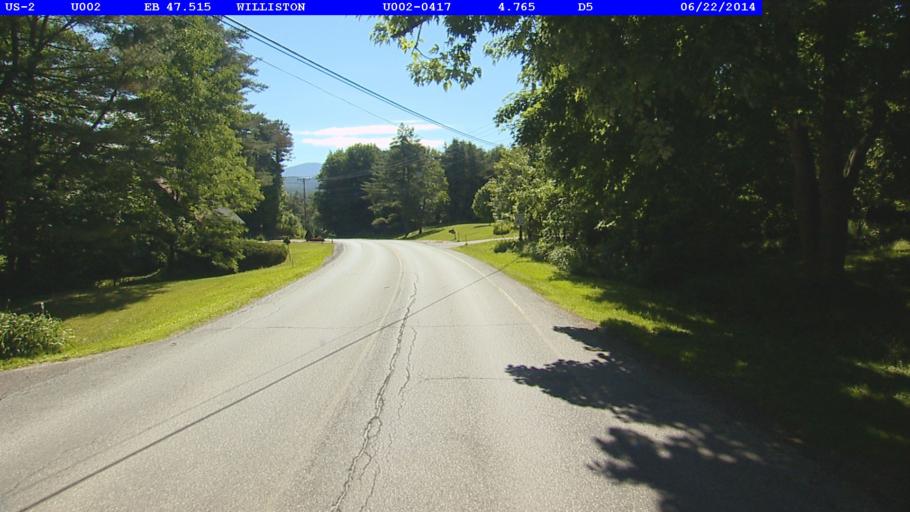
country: US
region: Vermont
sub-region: Chittenden County
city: Williston
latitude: 44.4342
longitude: -73.0481
